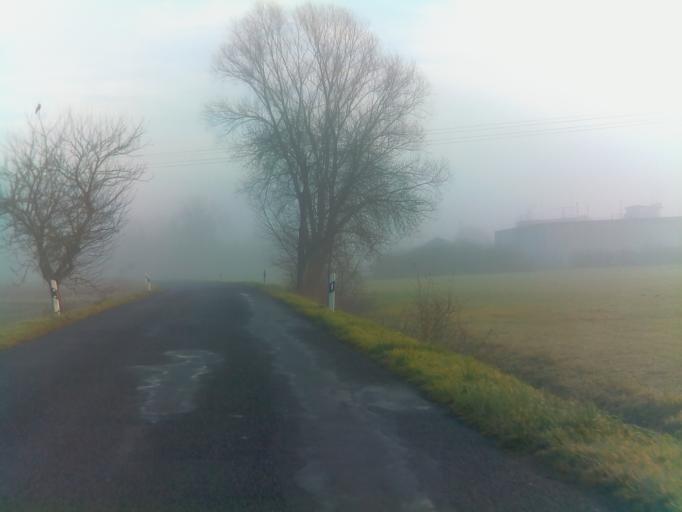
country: DE
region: Bavaria
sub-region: Regierungsbezirk Unterfranken
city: Neubrunn
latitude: 49.7599
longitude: 9.6505
